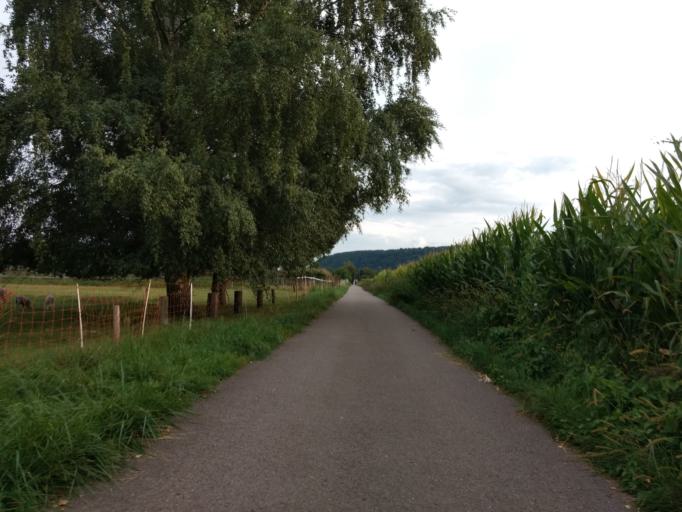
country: DE
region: Saarland
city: Dillingen
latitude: 49.3638
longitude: 6.7074
